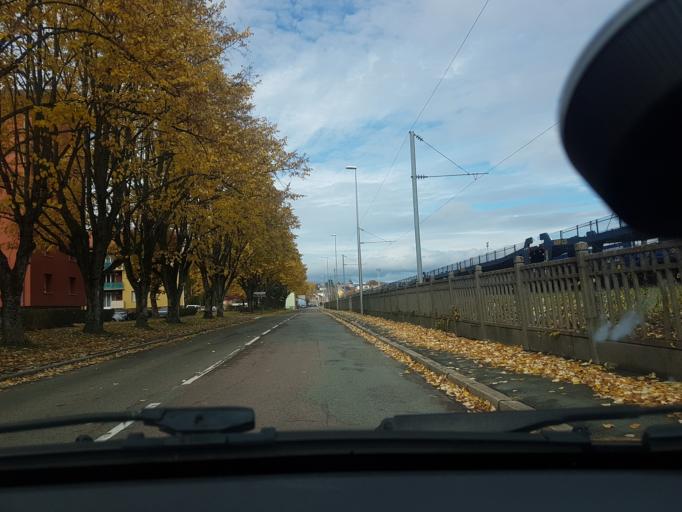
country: FR
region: Franche-Comte
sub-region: Territoire de Belfort
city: Belfort
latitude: 47.6291
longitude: 6.8539
